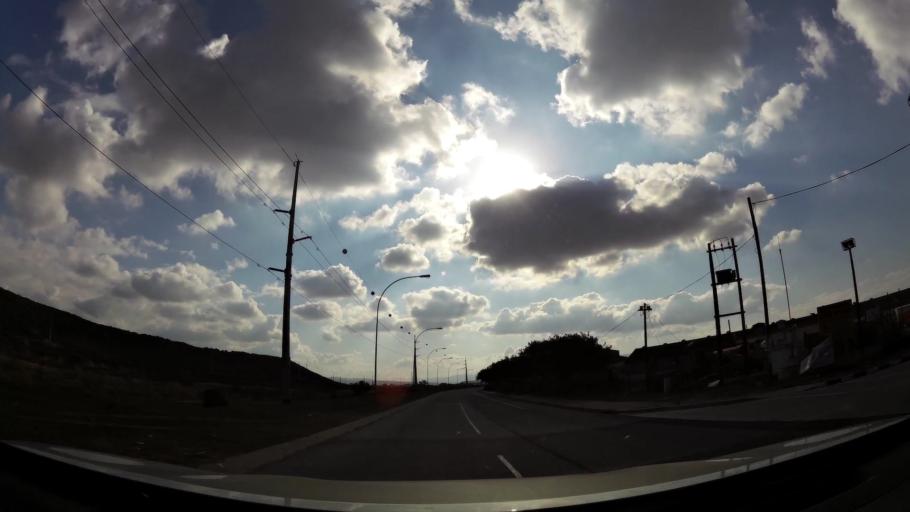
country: ZA
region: Eastern Cape
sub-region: Nelson Mandela Bay Metropolitan Municipality
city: Uitenhage
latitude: -33.7833
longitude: 25.3976
